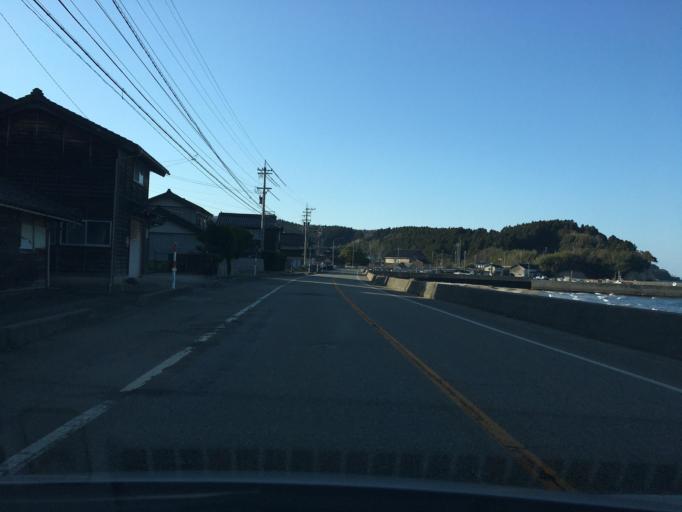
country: JP
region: Ishikawa
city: Nanao
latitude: 36.9753
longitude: 137.0507
